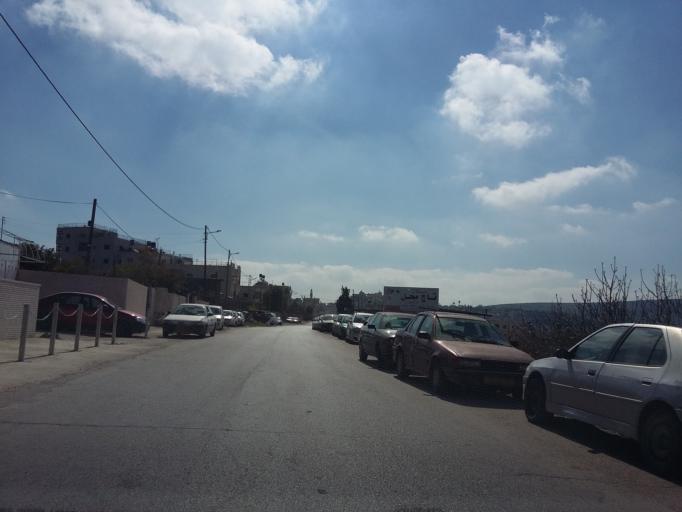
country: PS
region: West Bank
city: Al Jib
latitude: 31.8559
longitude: 35.1783
